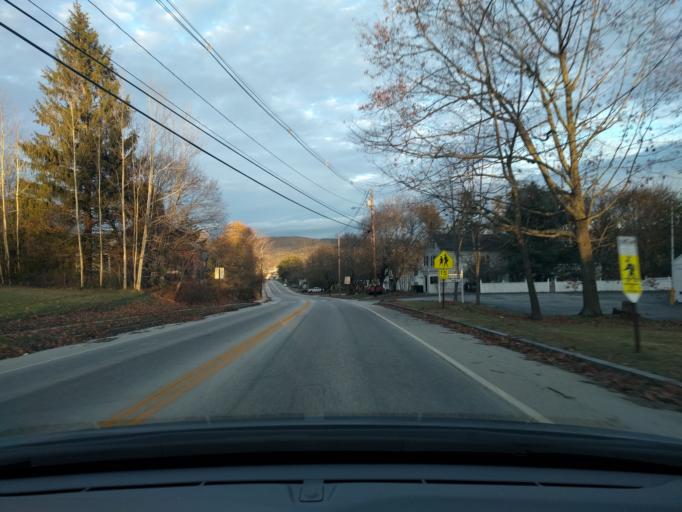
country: US
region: Maine
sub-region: Waldo County
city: Winterport
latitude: 44.6312
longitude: -68.8541
